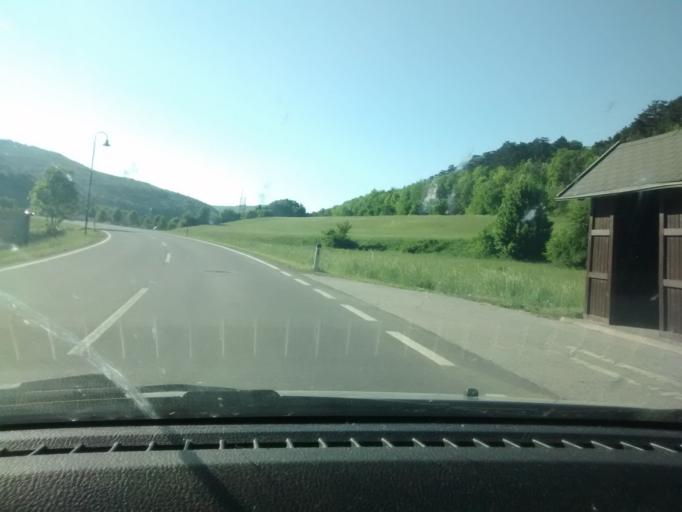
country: AT
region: Lower Austria
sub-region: Politischer Bezirk Baden
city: Alland
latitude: 48.0609
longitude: 16.0734
